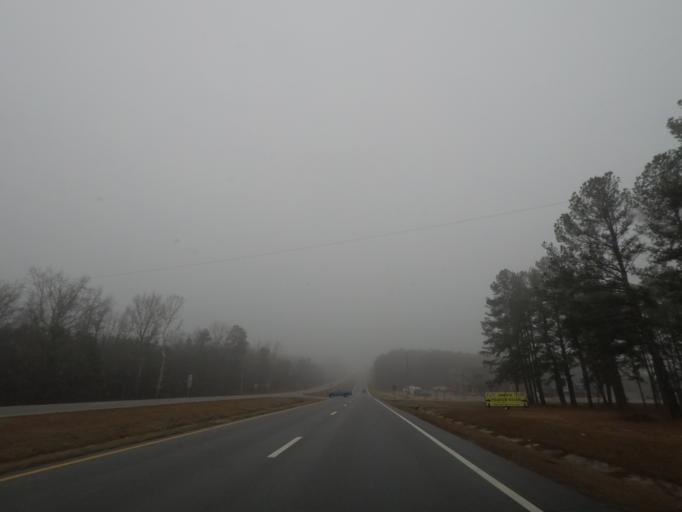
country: US
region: North Carolina
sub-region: Lee County
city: Sanford
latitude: 35.4025
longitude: -79.2316
